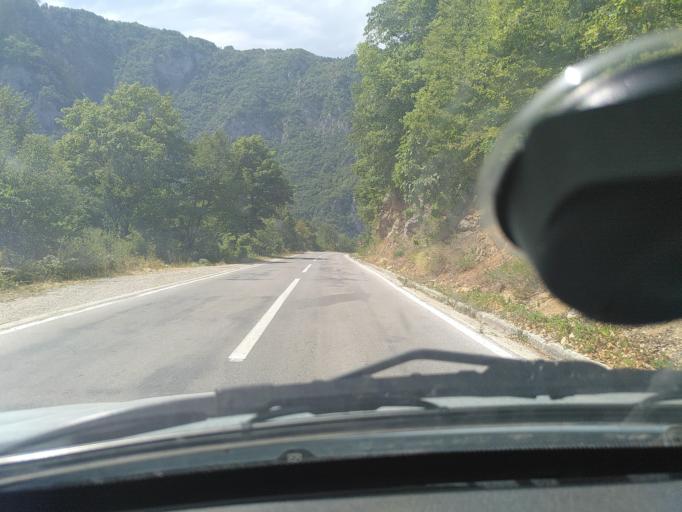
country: ME
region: Opstina Pluzine
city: Pluzine
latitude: 43.2198
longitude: 18.8522
